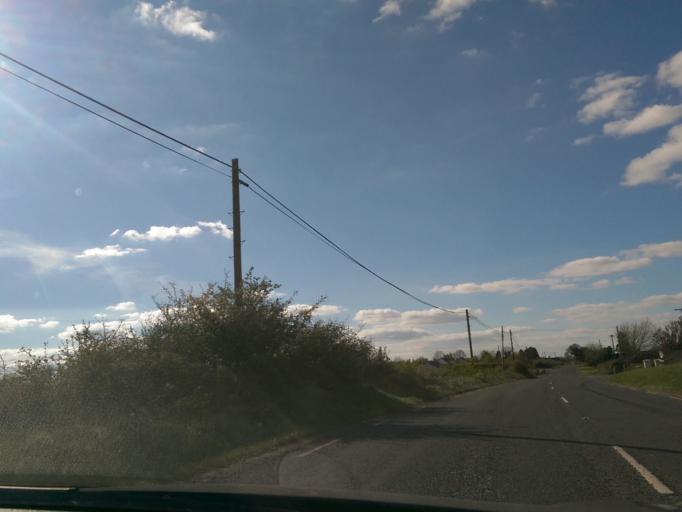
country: IE
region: Leinster
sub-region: Uibh Fhaili
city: Birr
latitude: 53.0936
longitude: -7.9635
